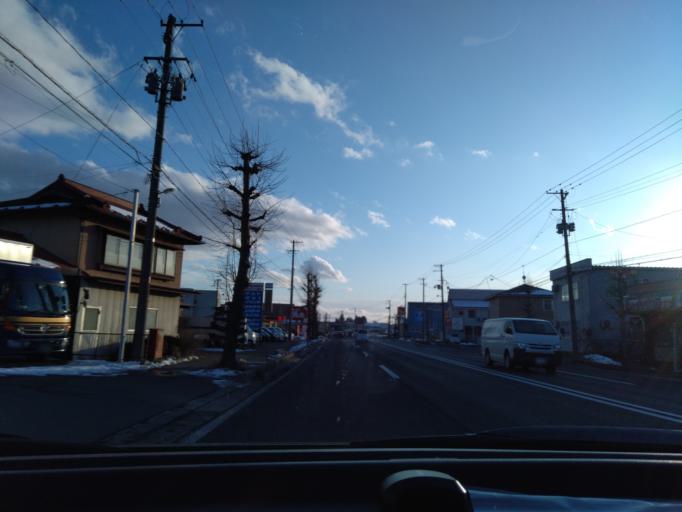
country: JP
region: Iwate
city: Morioka-shi
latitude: 39.6261
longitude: 141.1746
